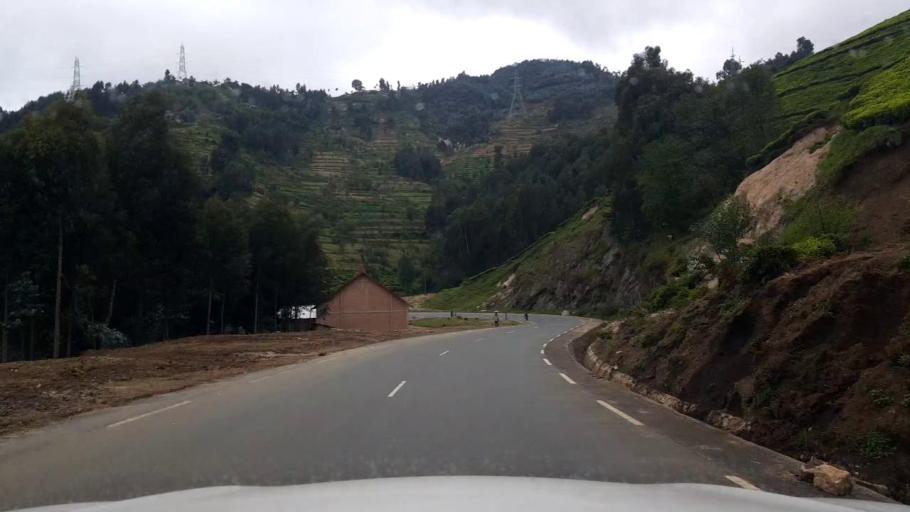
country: RW
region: Northern Province
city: Musanze
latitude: -1.6614
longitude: 29.5116
